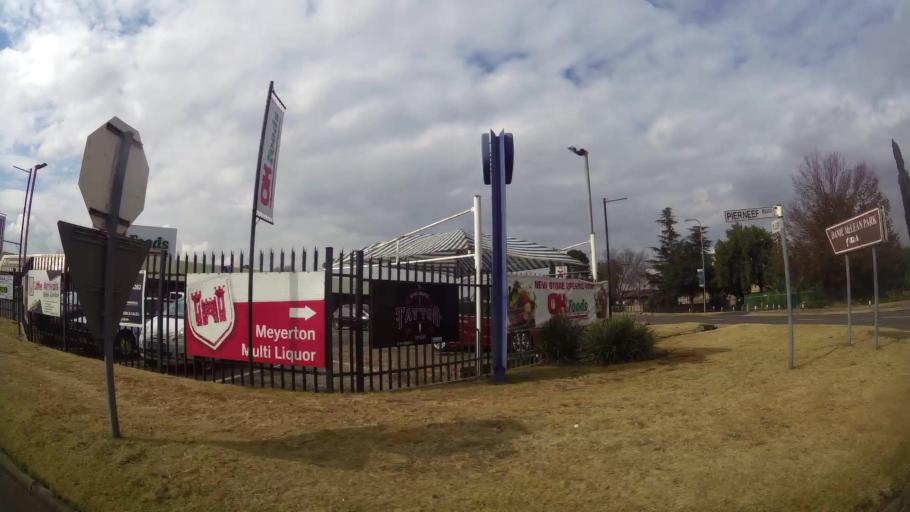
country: ZA
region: Gauteng
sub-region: Sedibeng District Municipality
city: Meyerton
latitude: -26.5961
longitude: 27.9913
